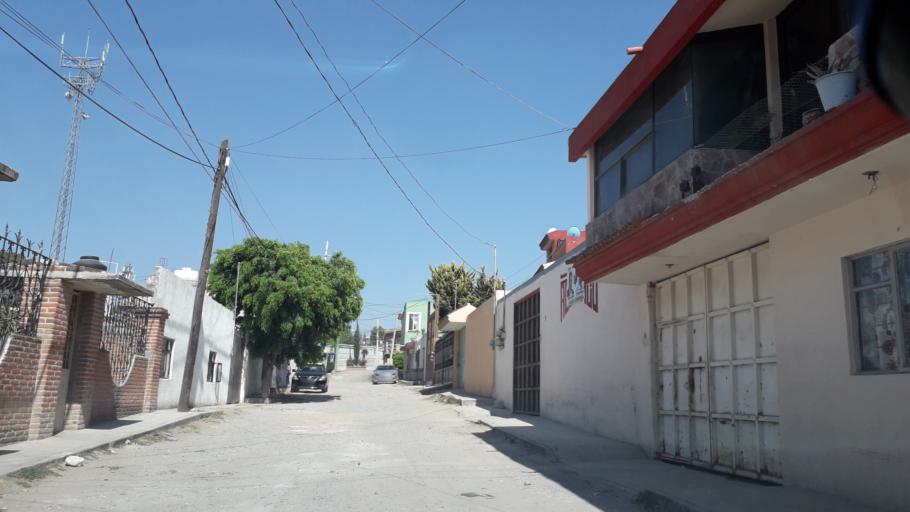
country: MX
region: Puebla
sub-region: Puebla
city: El Capulo (La Quebradora)
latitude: 18.9769
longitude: -98.2200
